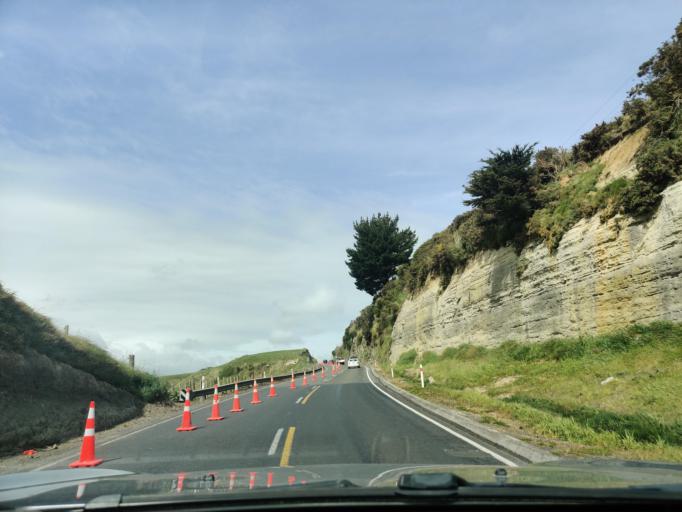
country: NZ
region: Taranaki
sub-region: South Taranaki District
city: Hawera
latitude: -39.6183
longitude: 174.3458
